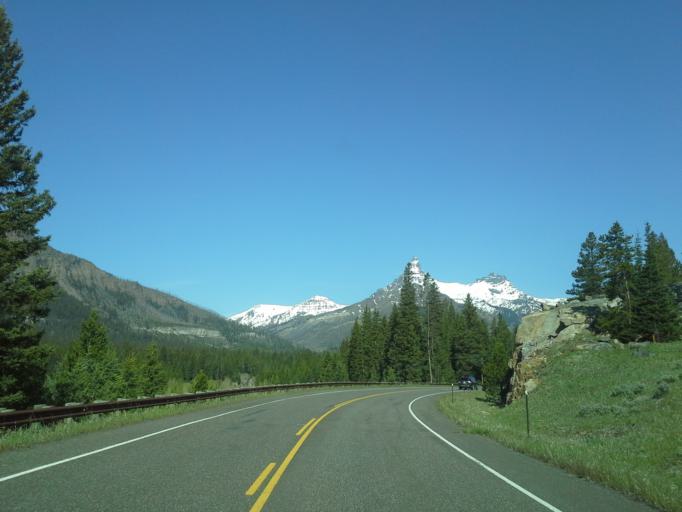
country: US
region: Montana
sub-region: Carbon County
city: Red Lodge
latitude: 44.9497
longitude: -109.7912
